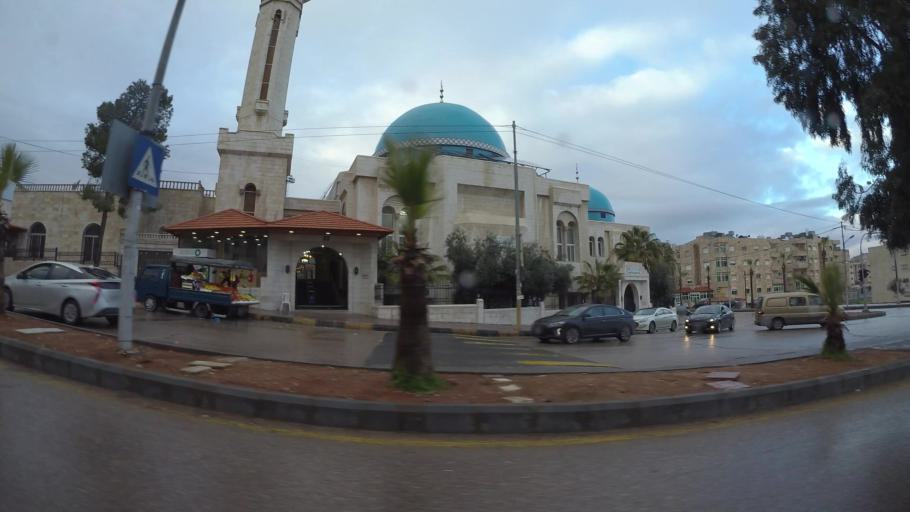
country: JO
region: Amman
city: Amman
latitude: 31.9788
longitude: 35.9103
